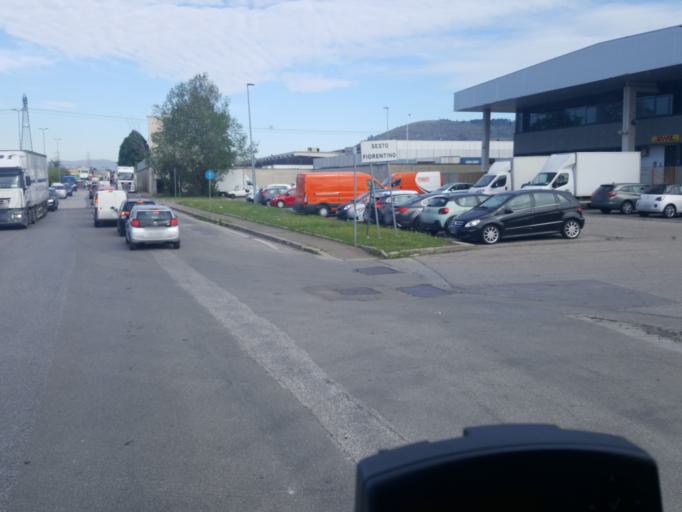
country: IT
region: Tuscany
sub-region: Province of Florence
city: Calenzano
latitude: 43.8427
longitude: 11.1626
